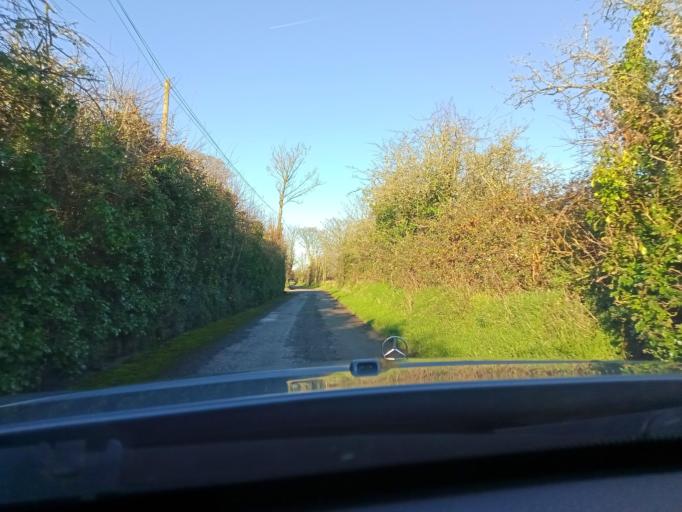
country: IE
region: Leinster
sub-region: Kilkenny
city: Mooncoin
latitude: 52.2920
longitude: -7.2059
